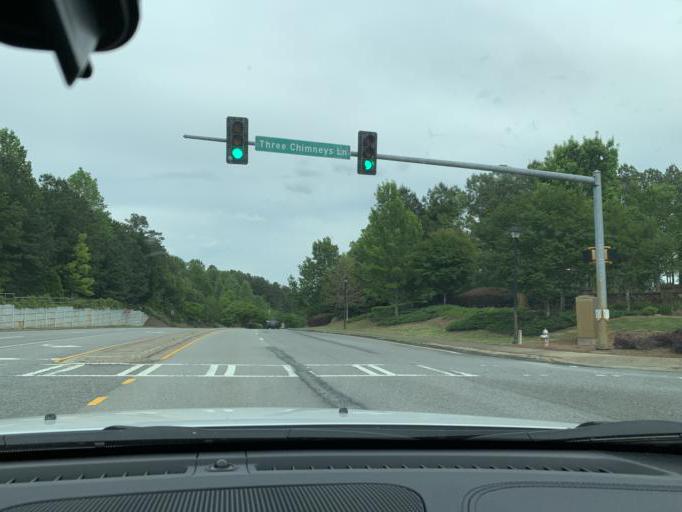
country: US
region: Georgia
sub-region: Forsyth County
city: Cumming
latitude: 34.1194
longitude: -84.1467
